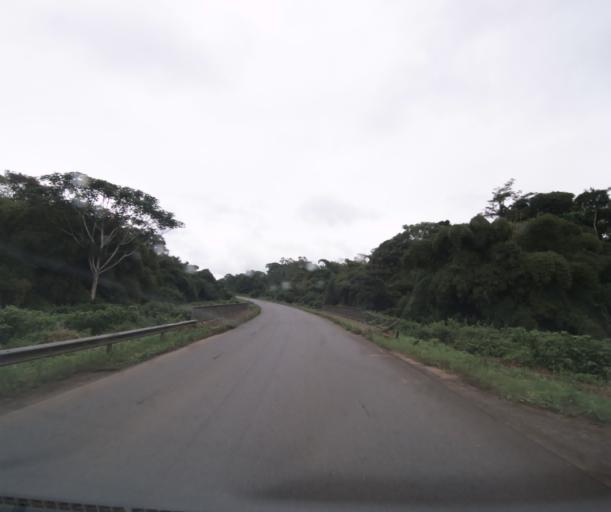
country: CM
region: Littoral
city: Edea
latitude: 3.7202
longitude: 10.1074
